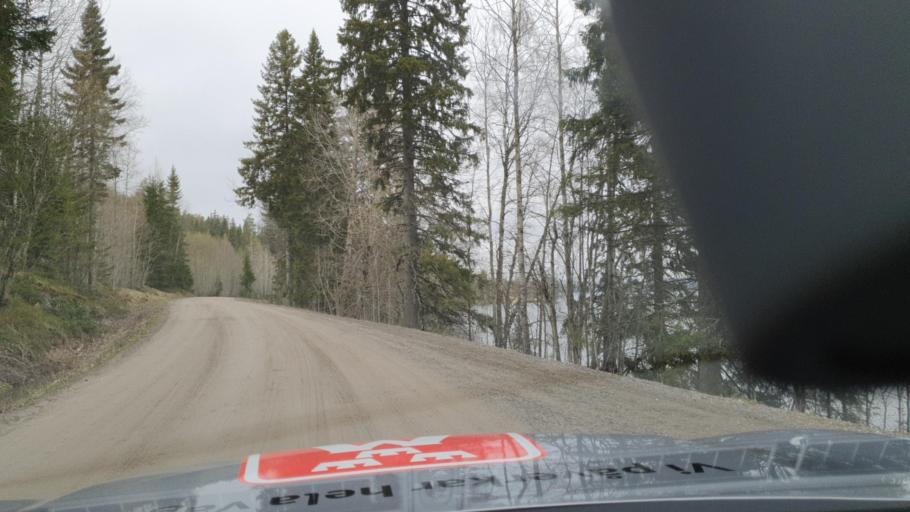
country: SE
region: Vaesternorrland
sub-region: OErnskoeldsviks Kommun
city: Husum
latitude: 63.6331
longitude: 19.0605
